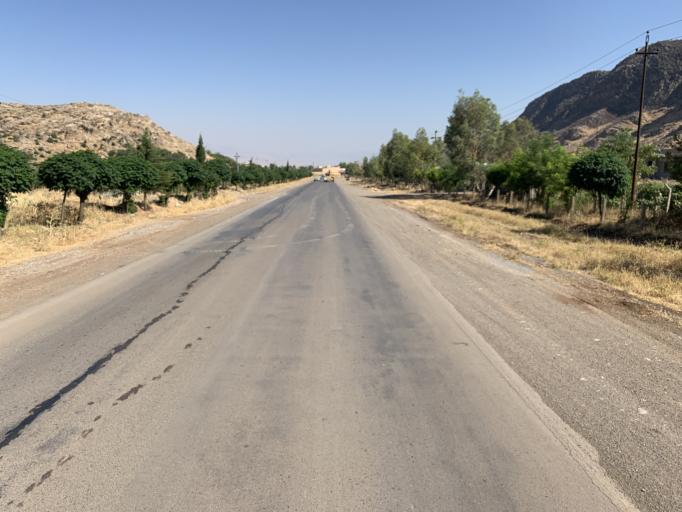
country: IQ
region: As Sulaymaniyah
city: Raniye
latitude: 36.2705
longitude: 44.8365
